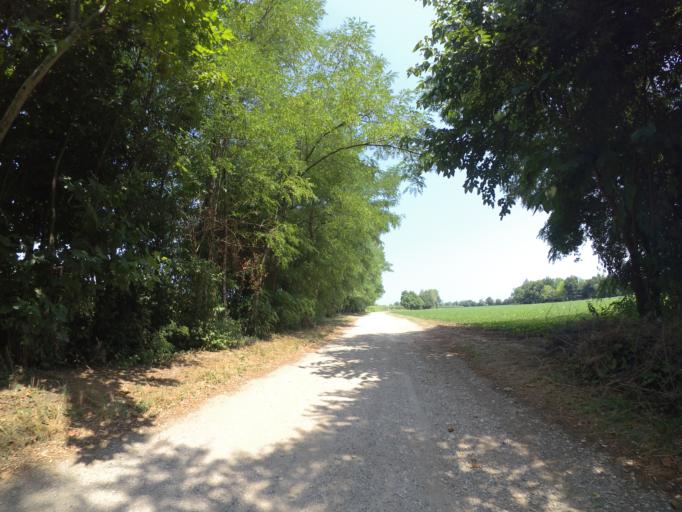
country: IT
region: Friuli Venezia Giulia
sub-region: Provincia di Udine
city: Basiliano
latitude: 45.9836
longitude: 13.0724
